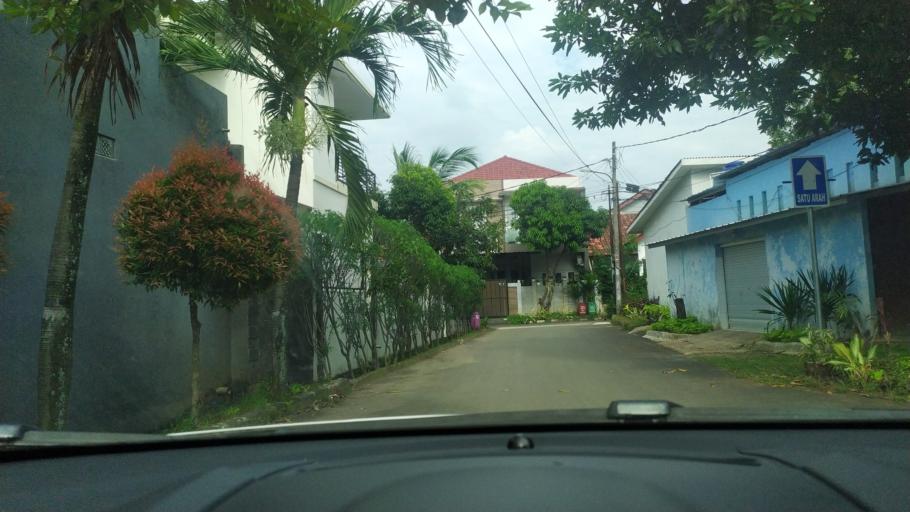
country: ID
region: West Java
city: Pamulang
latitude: -6.3553
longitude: 106.7450
